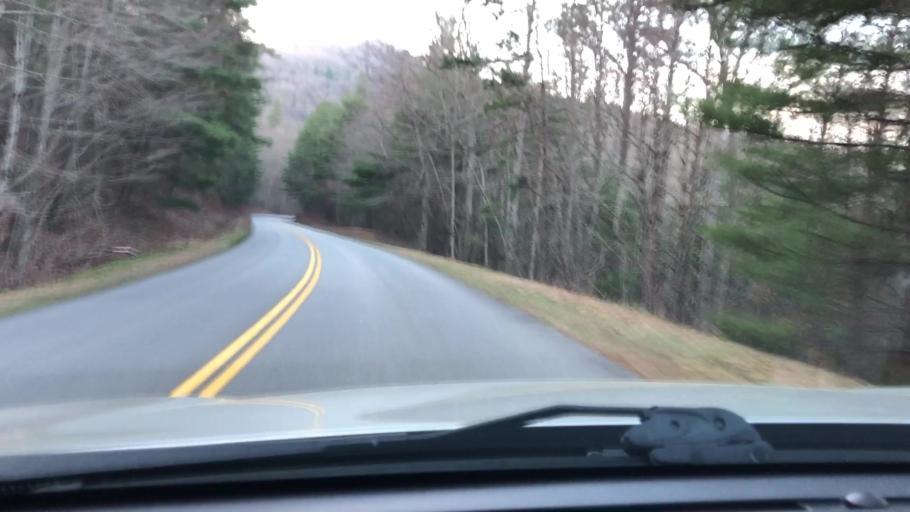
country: US
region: North Carolina
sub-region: Buncombe County
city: Biltmore Forest
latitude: 35.5444
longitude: -82.4995
